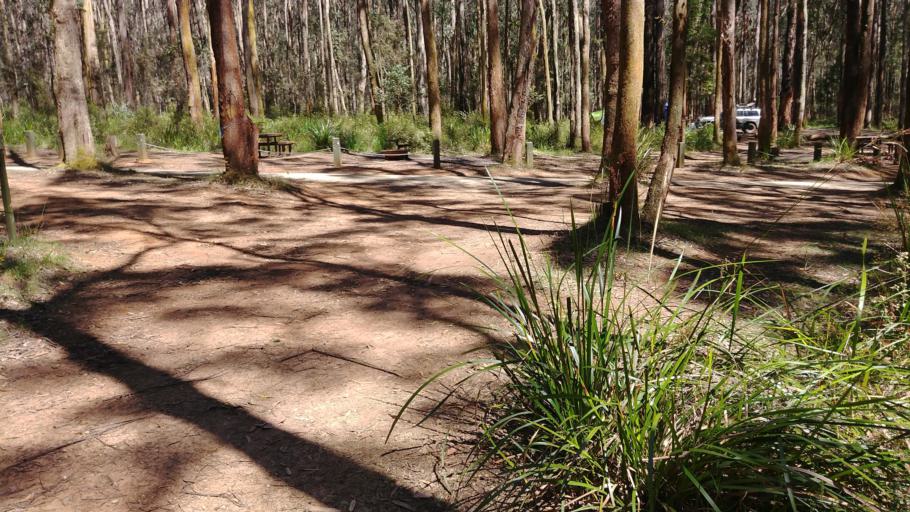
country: AU
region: Victoria
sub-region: Cardinia
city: Gembrook
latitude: -37.8980
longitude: 145.5842
